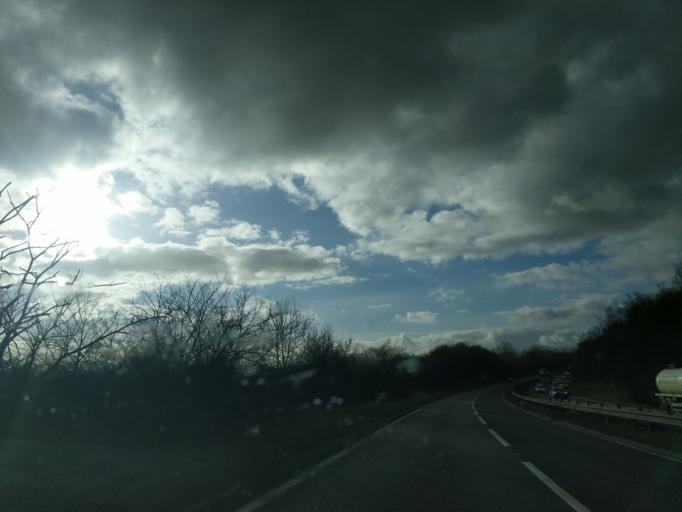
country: GB
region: England
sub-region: Derbyshire
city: Pinxton
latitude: 53.0940
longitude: -1.3320
